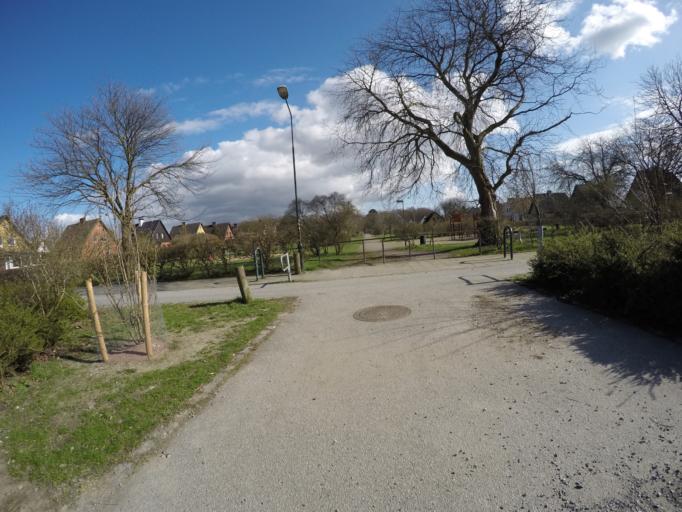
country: SE
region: Skane
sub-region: Burlovs Kommun
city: Arloev
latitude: 55.6130
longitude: 13.0448
